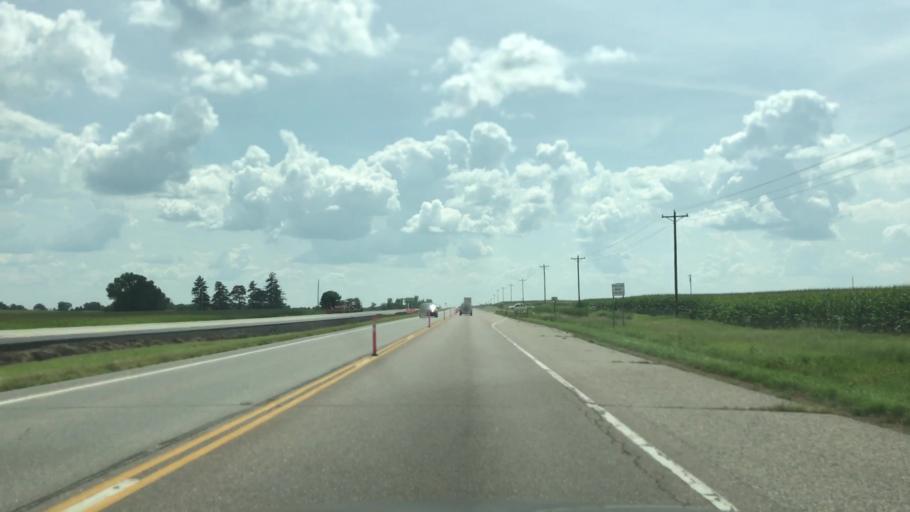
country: US
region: Minnesota
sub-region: Scott County
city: Belle Plaine
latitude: 44.5721
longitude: -93.8427
